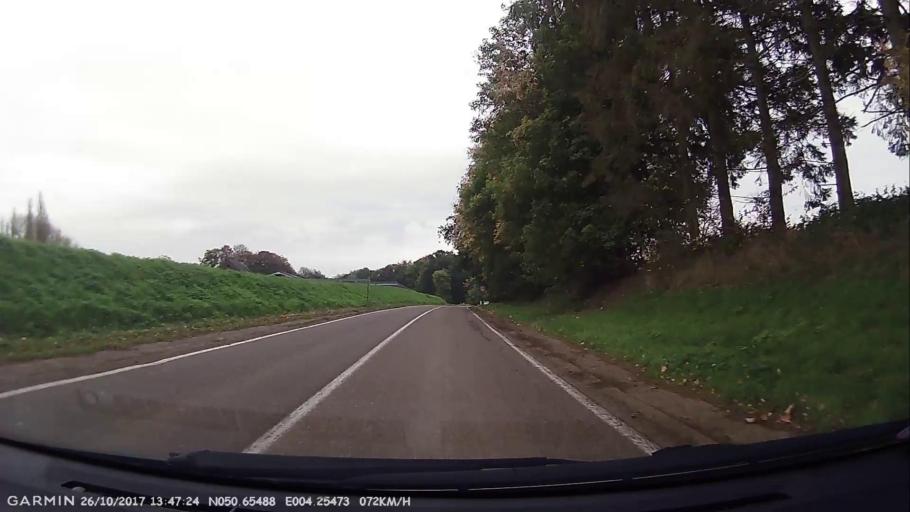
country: BE
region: Wallonia
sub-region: Province du Brabant Wallon
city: Ittre
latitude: 50.6548
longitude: 4.2549
